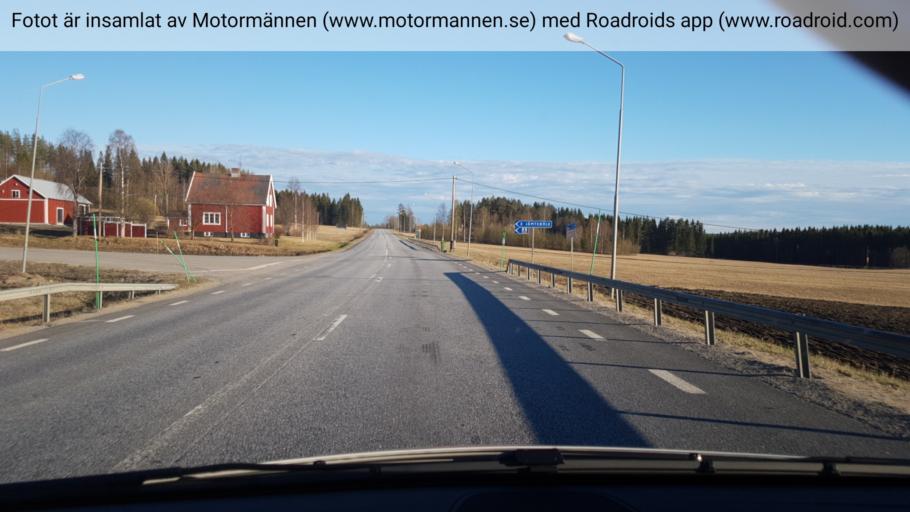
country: SE
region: Vaesterbotten
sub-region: Vannas Kommun
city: Vaennaes
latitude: 63.9839
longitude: 19.7289
